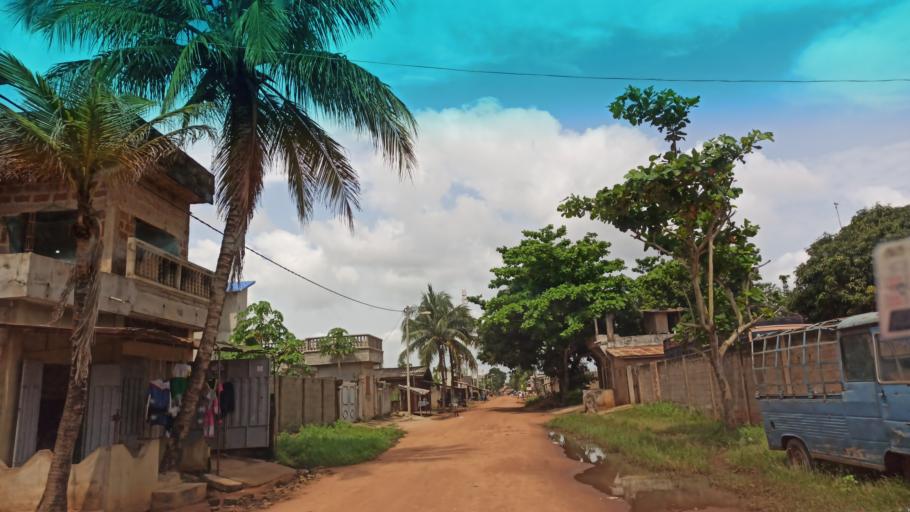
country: BJ
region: Queme
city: Porto-Novo
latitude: 6.4985
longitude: 2.5883
